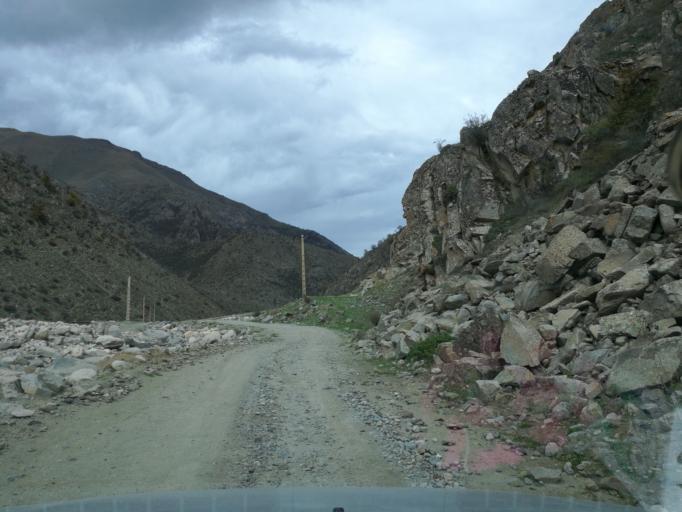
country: IR
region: Mazandaran
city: `Abbasabad
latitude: 36.4303
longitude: 51.0416
